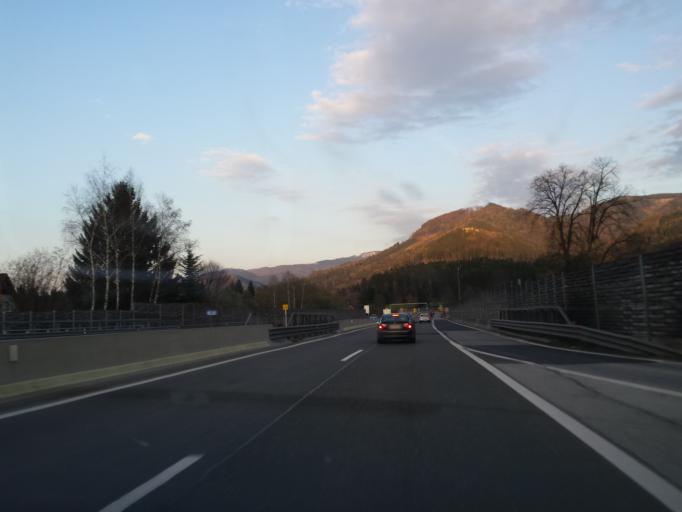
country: AT
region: Styria
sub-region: Politischer Bezirk Bruck-Muerzzuschlag
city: Langenwang
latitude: 47.5584
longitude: 15.5947
